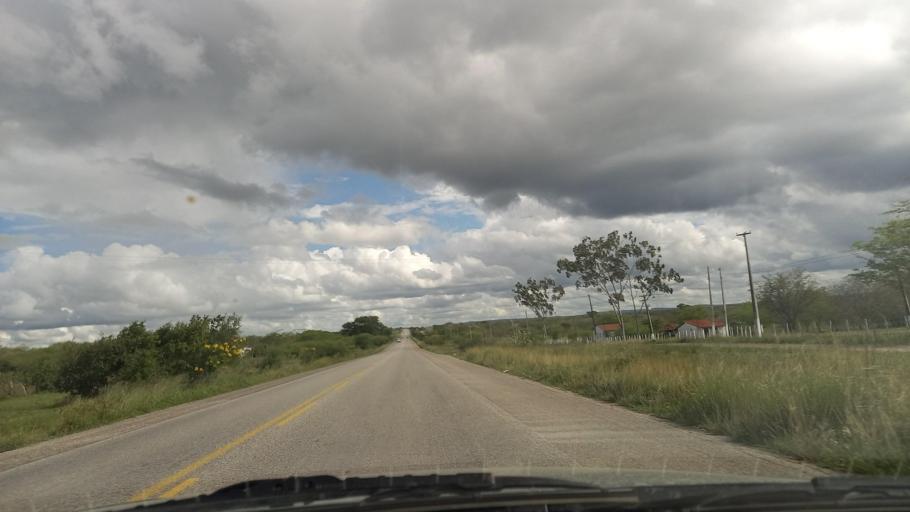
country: BR
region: Pernambuco
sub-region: Cachoeirinha
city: Cachoeirinha
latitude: -8.5100
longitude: -36.2517
